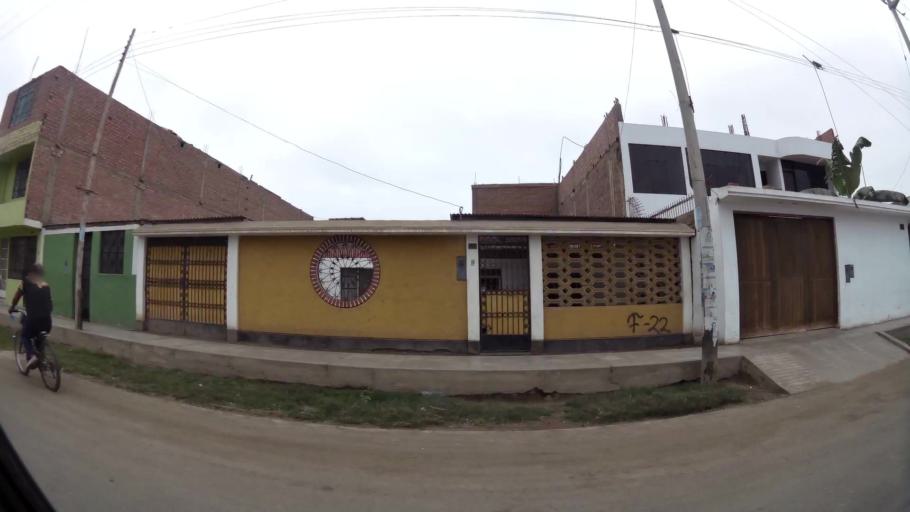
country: PE
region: Lima
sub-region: Barranca
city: Paramonga
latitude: -10.6789
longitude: -77.8172
